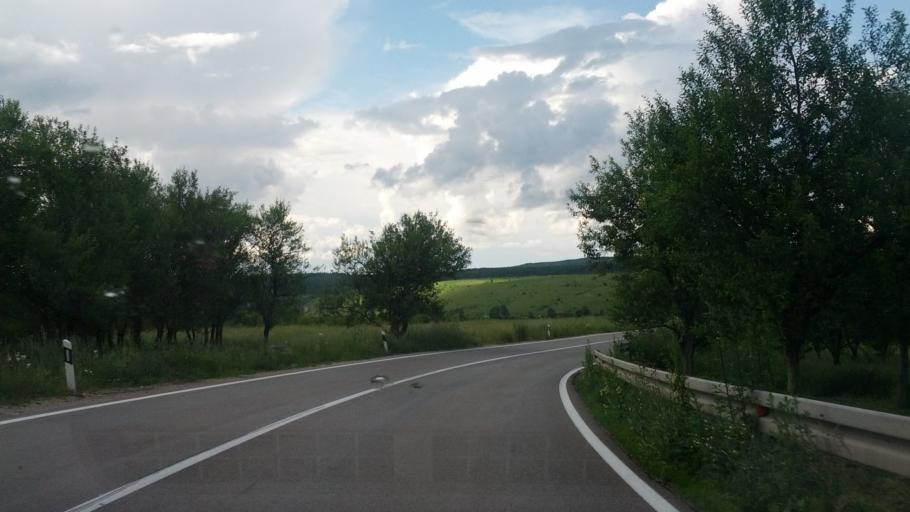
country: BA
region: Federation of Bosnia and Herzegovina
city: Izacic
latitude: 44.9079
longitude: 15.7187
